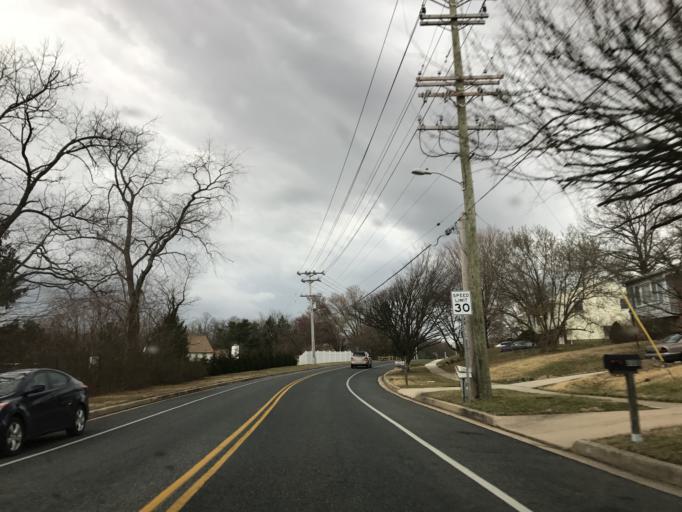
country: US
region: Maryland
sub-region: Harford County
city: South Bel Air
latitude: 39.5306
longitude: -76.3315
